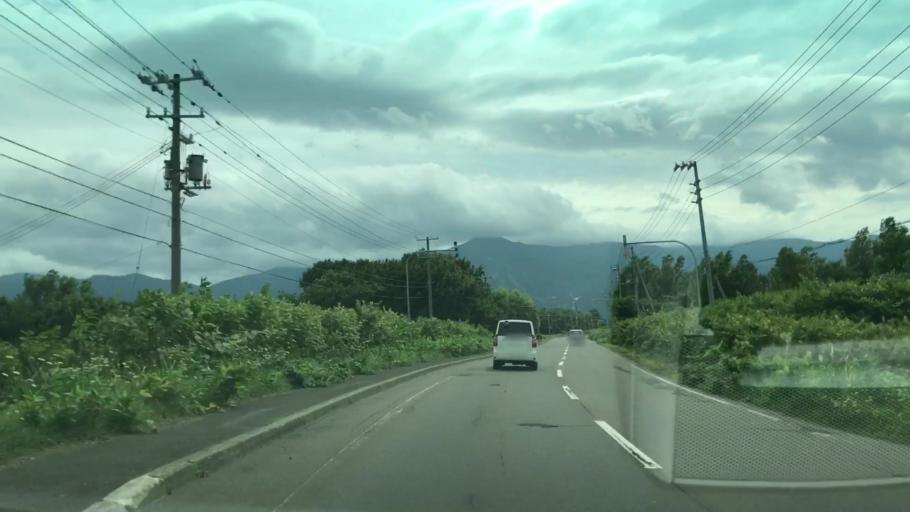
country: JP
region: Hokkaido
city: Iwanai
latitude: 43.0049
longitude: 140.5424
